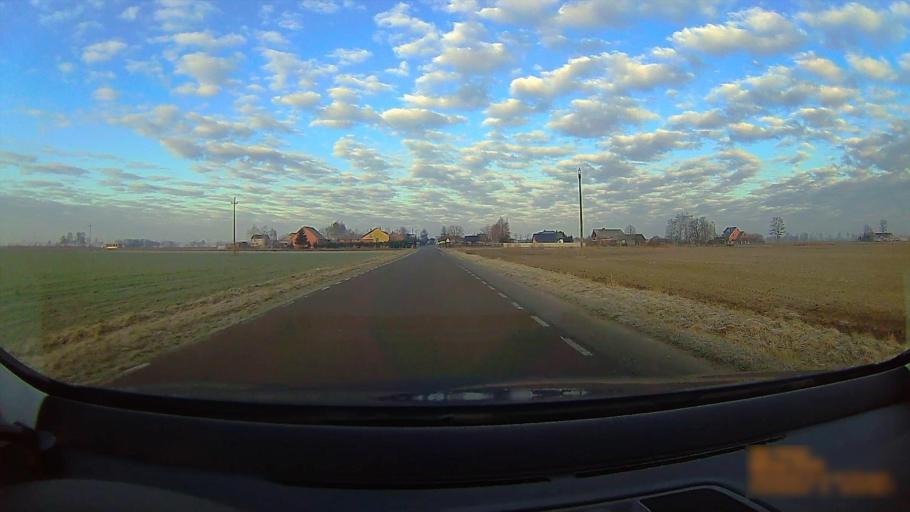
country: PL
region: Greater Poland Voivodeship
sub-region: Powiat koninski
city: Rychwal
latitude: 52.0974
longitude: 18.1212
